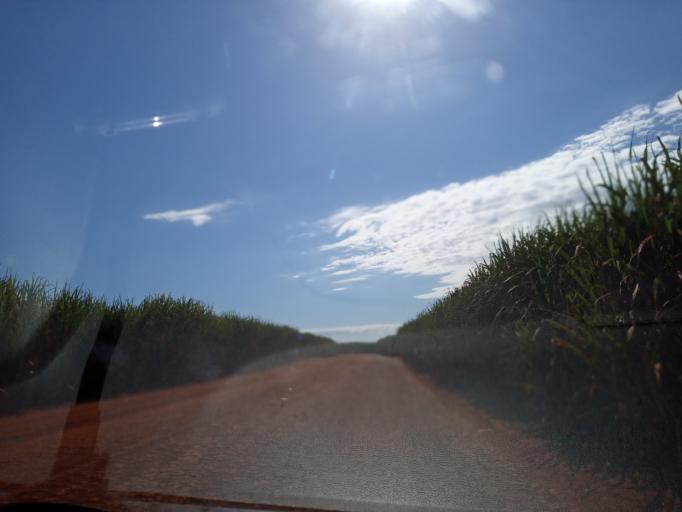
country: BR
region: Goias
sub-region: Itumbiara
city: Itumbiara
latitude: -18.4501
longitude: -49.1804
